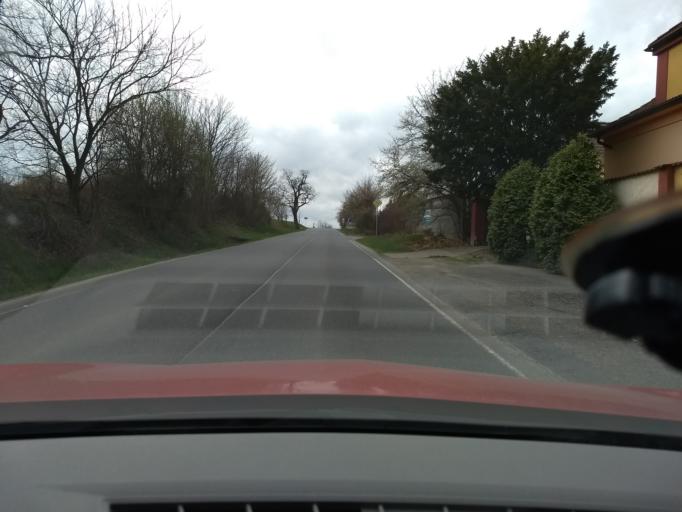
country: CZ
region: Central Bohemia
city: Unhost'
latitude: 50.0820
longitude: 14.1397
